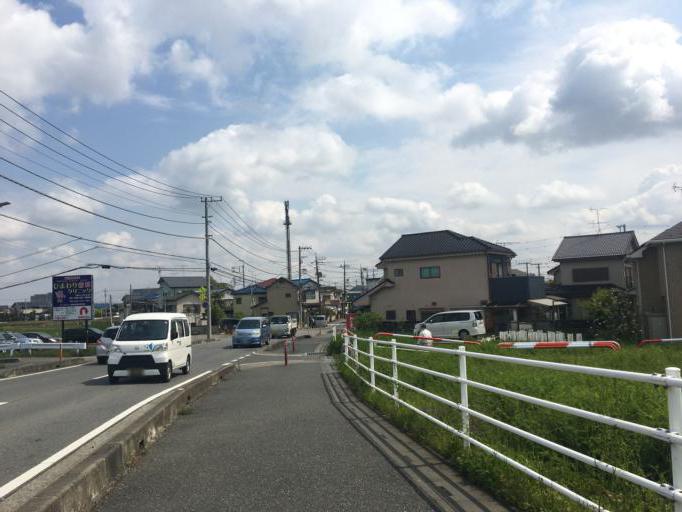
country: JP
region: Saitama
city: Kamifukuoka
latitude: 35.8926
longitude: 139.5055
